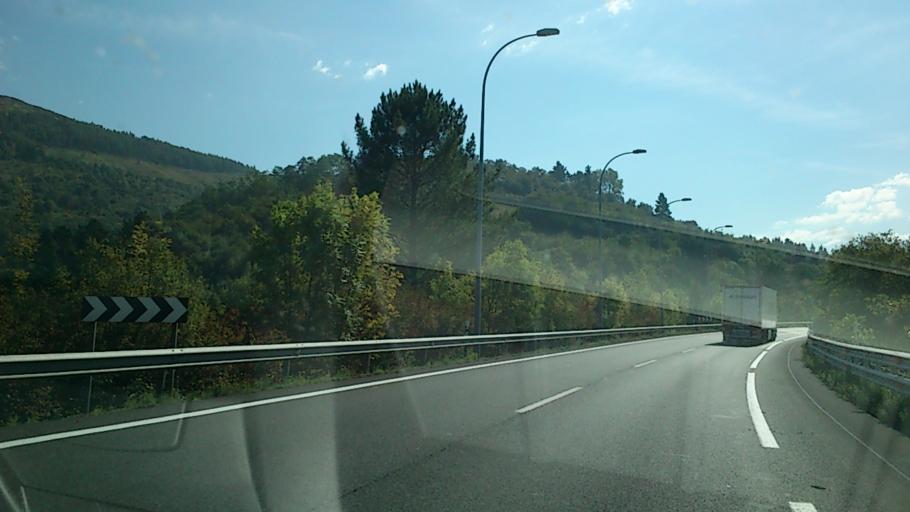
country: ES
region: Basque Country
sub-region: Bizkaia
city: Santutxu
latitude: 43.2321
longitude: -2.9149
